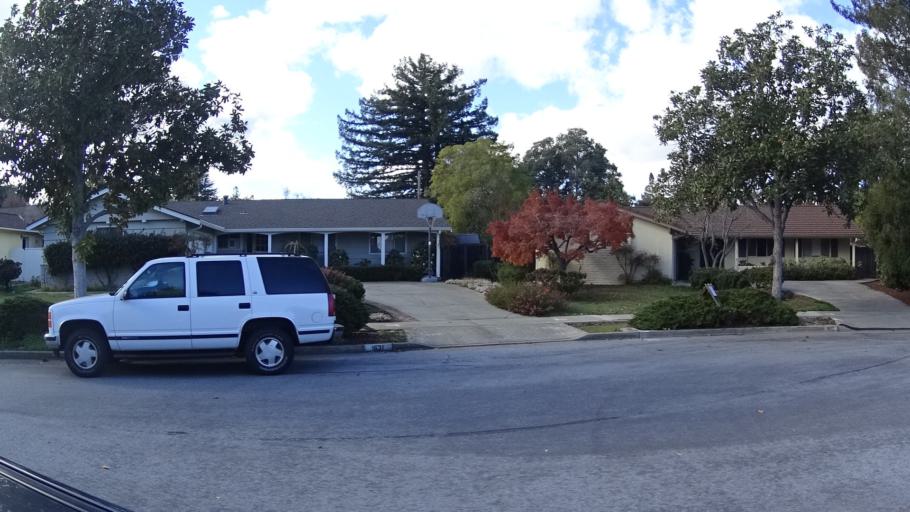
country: US
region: California
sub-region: Santa Clara County
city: Cupertino
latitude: 37.3394
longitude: -122.0531
